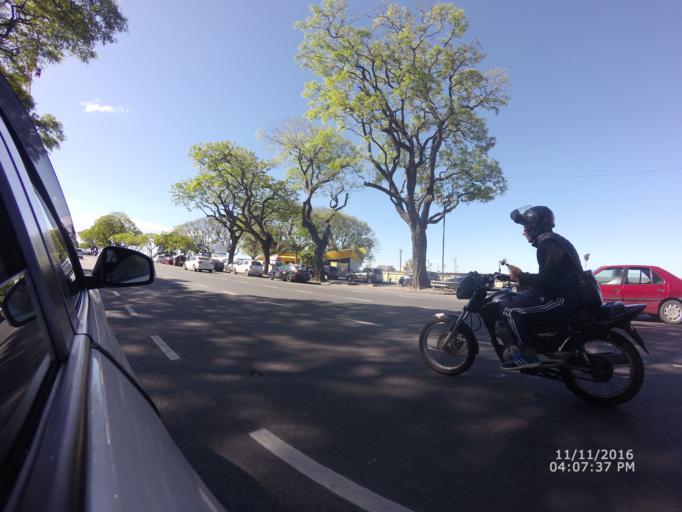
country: AR
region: Buenos Aires F.D.
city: Retiro
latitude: -34.5584
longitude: -58.4103
